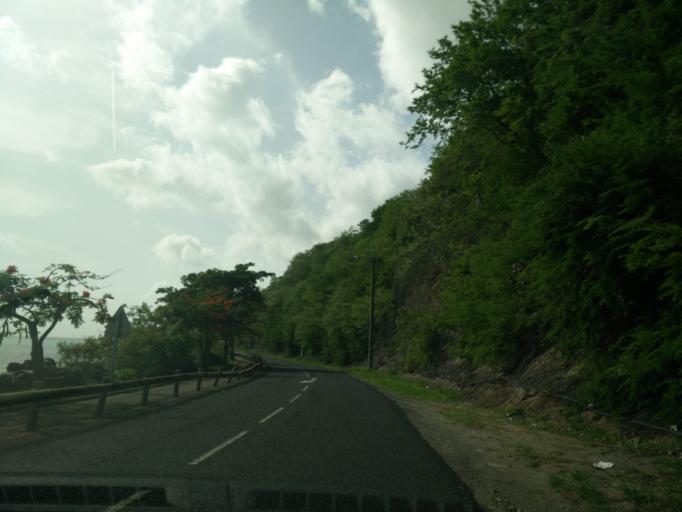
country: MQ
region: Martinique
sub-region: Martinique
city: Saint-Pierre
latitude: 14.7876
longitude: -61.2175
